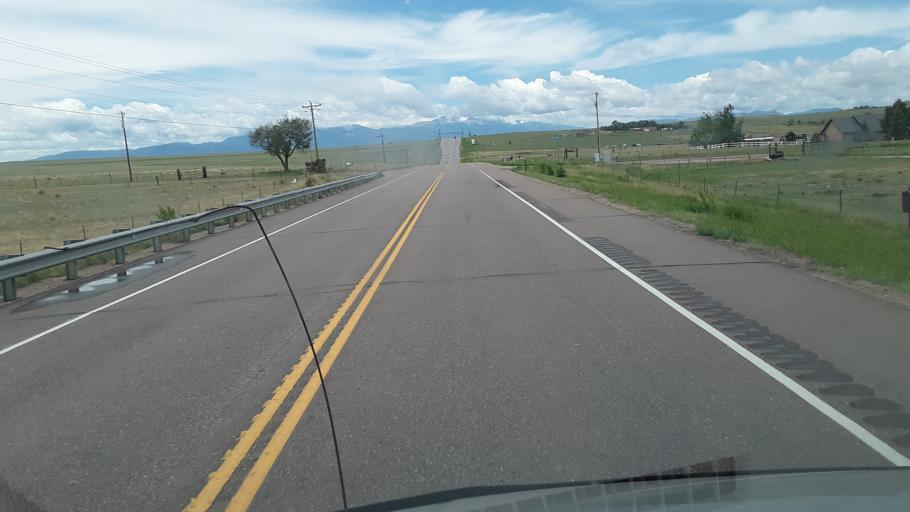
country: US
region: Colorado
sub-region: El Paso County
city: Ellicott
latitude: 38.8387
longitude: -104.5430
